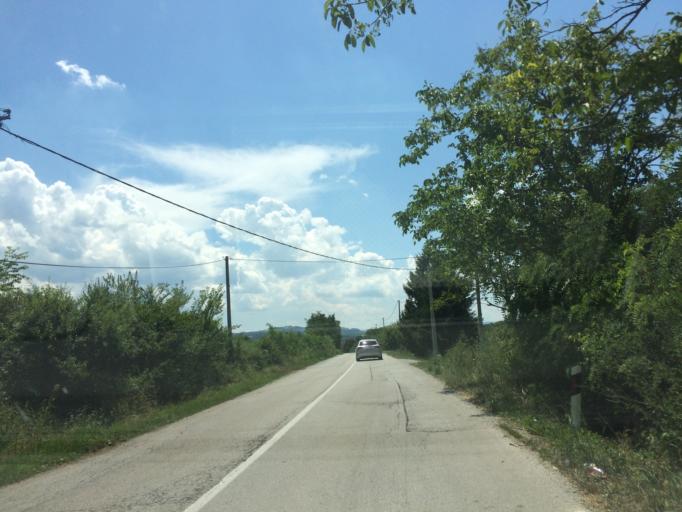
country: RS
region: Central Serbia
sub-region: Kolubarski Okrug
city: Ljig
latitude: 44.2337
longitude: 20.1833
